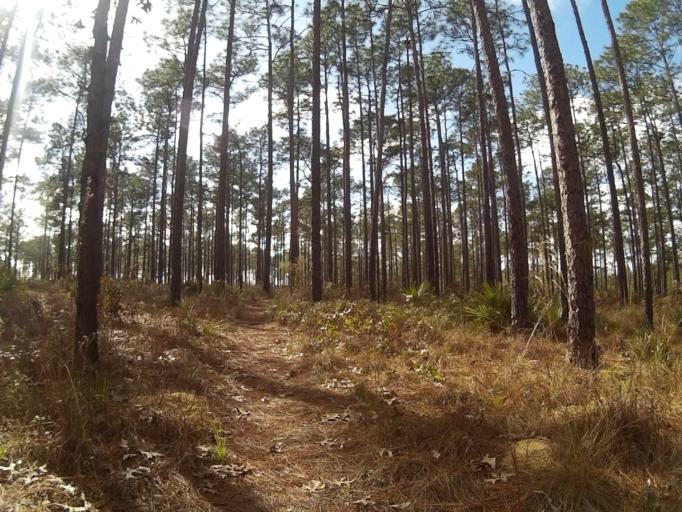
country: US
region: Florida
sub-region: Lake County
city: Astor
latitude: 29.0704
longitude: -81.6035
